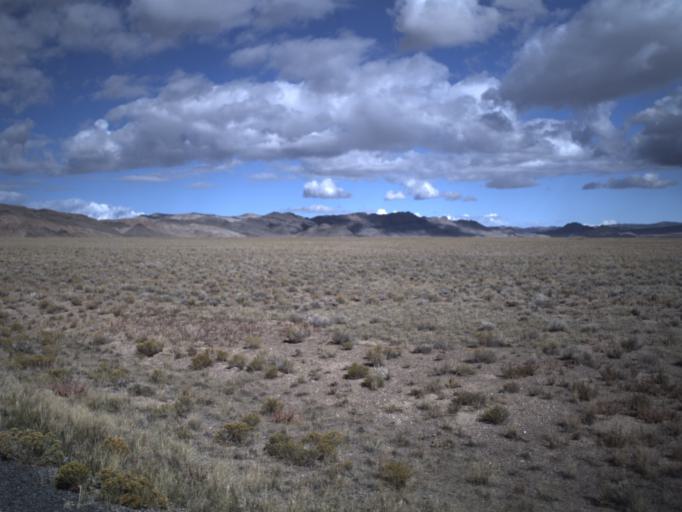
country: US
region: Utah
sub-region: Beaver County
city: Milford
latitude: 38.5630
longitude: -113.7648
